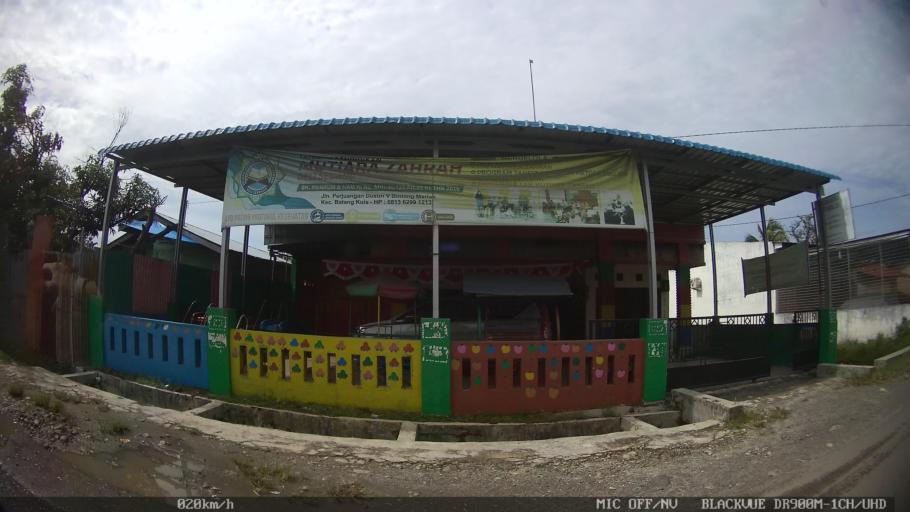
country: ID
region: North Sumatra
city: Percut
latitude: 3.6198
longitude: 98.7947
